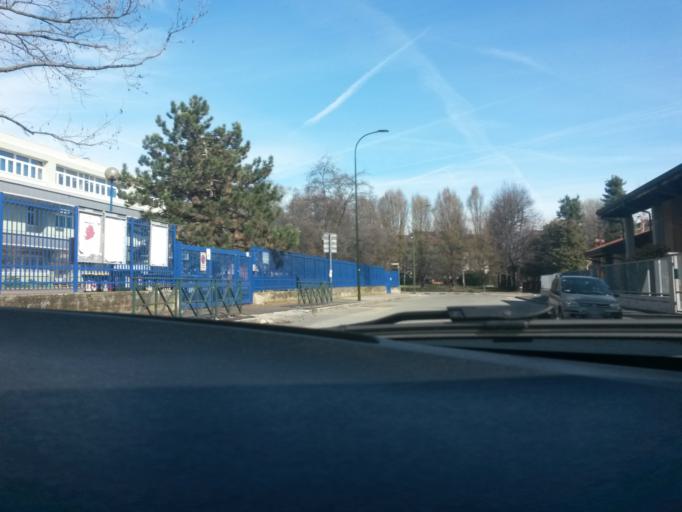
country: IT
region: Piedmont
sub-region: Provincia di Torino
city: Lesna
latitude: 45.0825
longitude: 7.6190
